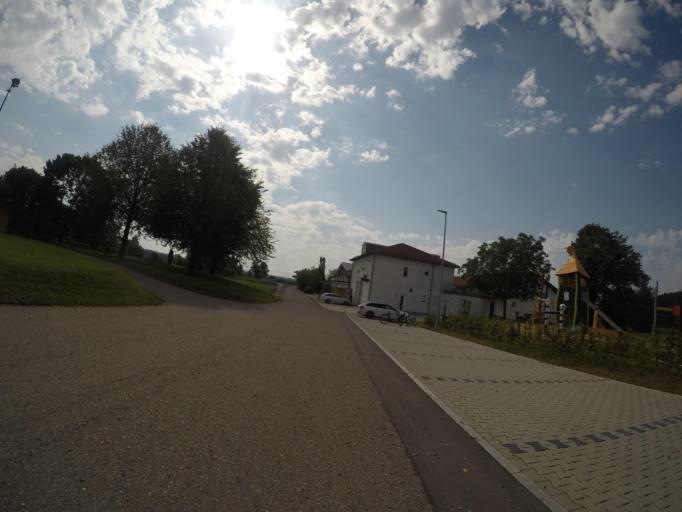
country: DE
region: Bavaria
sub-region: Swabia
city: Altenstadt
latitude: 48.1723
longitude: 10.0785
